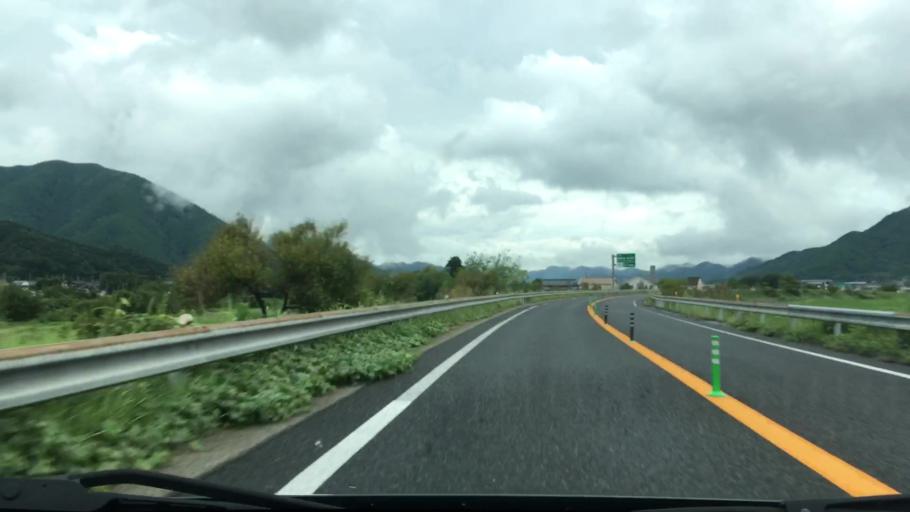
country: JP
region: Hyogo
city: Nishiwaki
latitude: 35.0650
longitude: 134.7679
